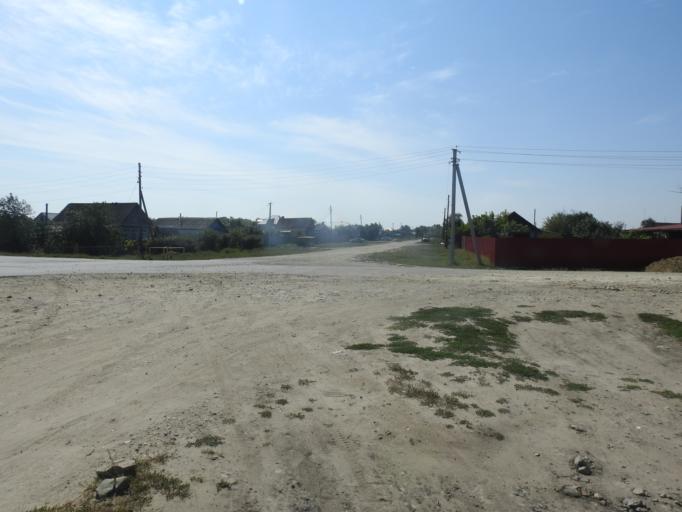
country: RU
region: Saratov
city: Lysyye Gory
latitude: 51.3303
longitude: 45.0694
